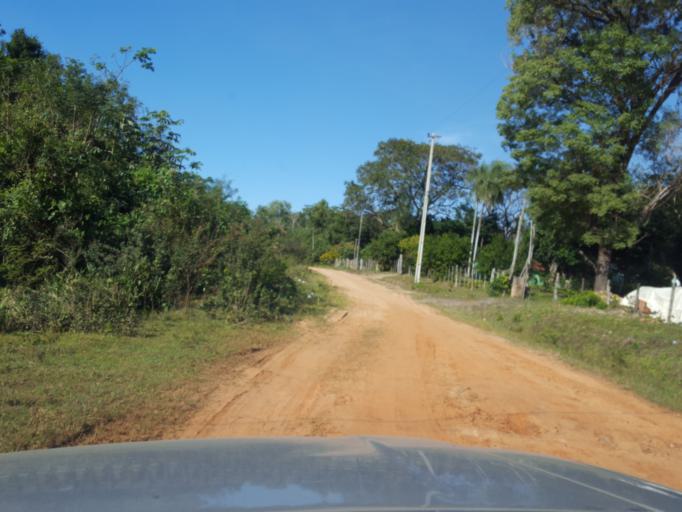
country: PY
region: Cordillera
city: Atyra
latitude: -25.2450
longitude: -57.1327
